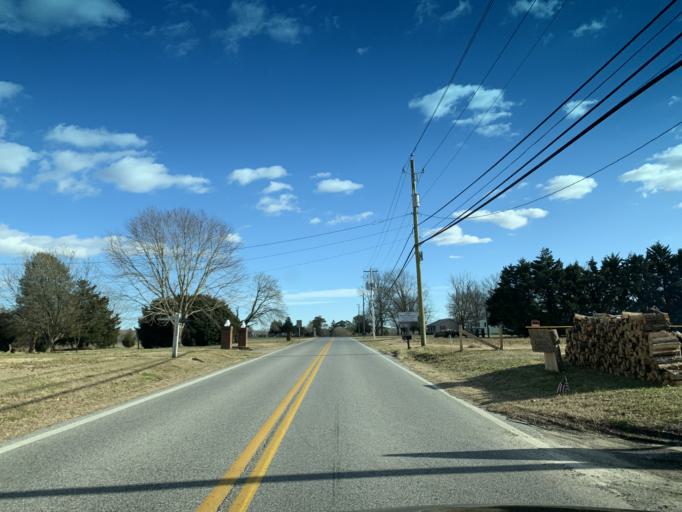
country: US
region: Maryland
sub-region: Worcester County
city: Berlin
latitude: 38.3202
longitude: -75.2011
